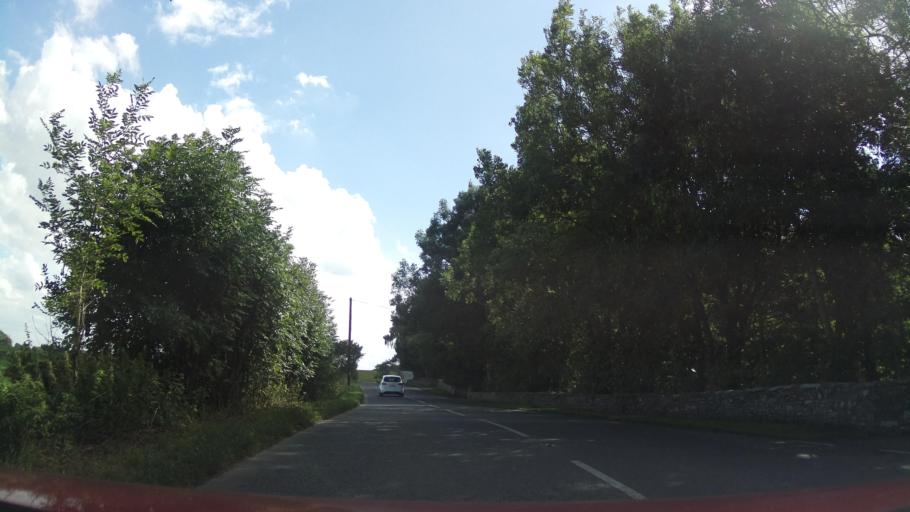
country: GB
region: England
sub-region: North Yorkshire
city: Leyburn
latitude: 54.3287
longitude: -1.8255
